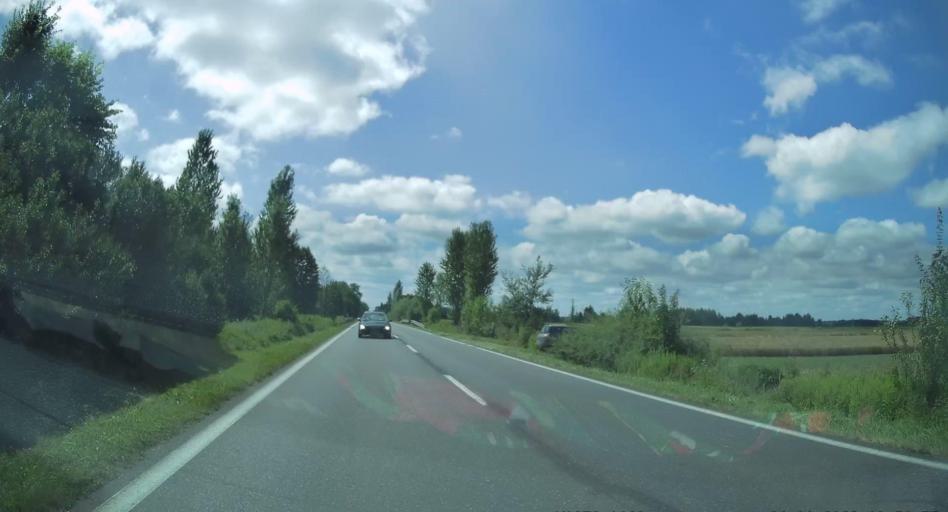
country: PL
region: Subcarpathian Voivodeship
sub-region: Powiat mielecki
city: Padew Narodowa
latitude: 50.4069
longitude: 21.4736
